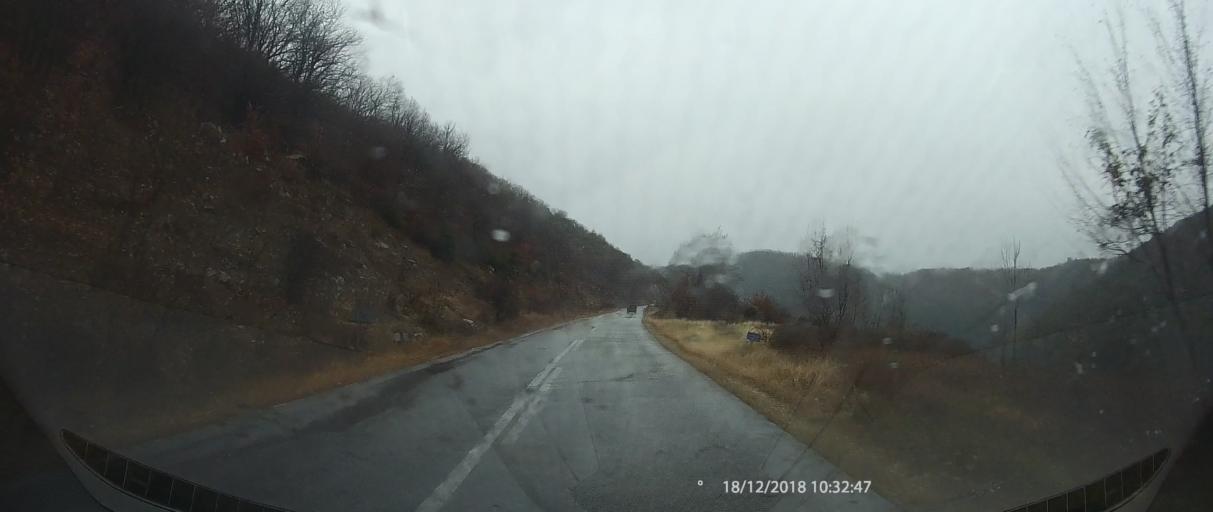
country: GR
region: Central Macedonia
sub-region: Nomos Pierias
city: Kato Milia
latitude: 40.1931
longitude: 22.2951
